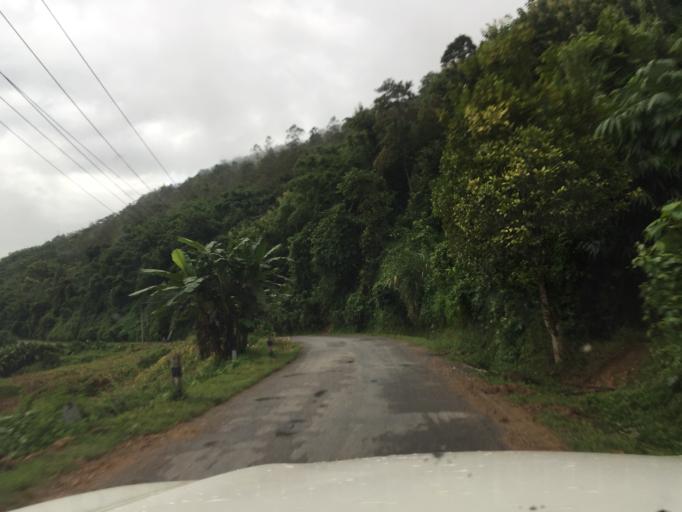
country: LA
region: Oudomxai
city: Muang La
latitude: 20.9061
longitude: 102.1804
